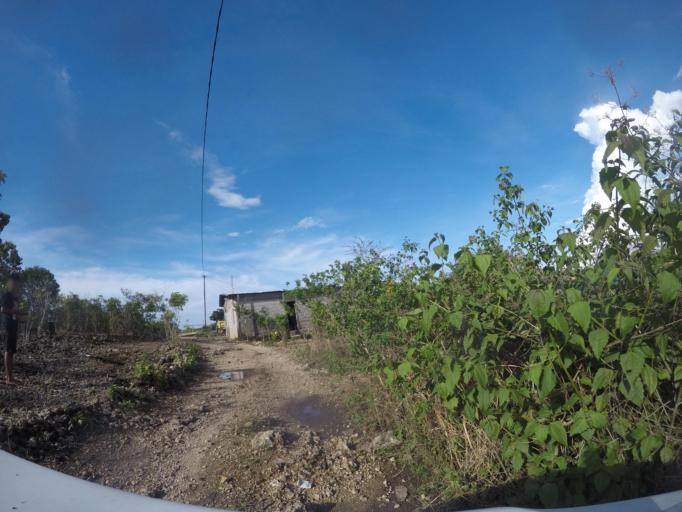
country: TL
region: Baucau
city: Baucau
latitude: -8.4896
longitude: 126.4533
